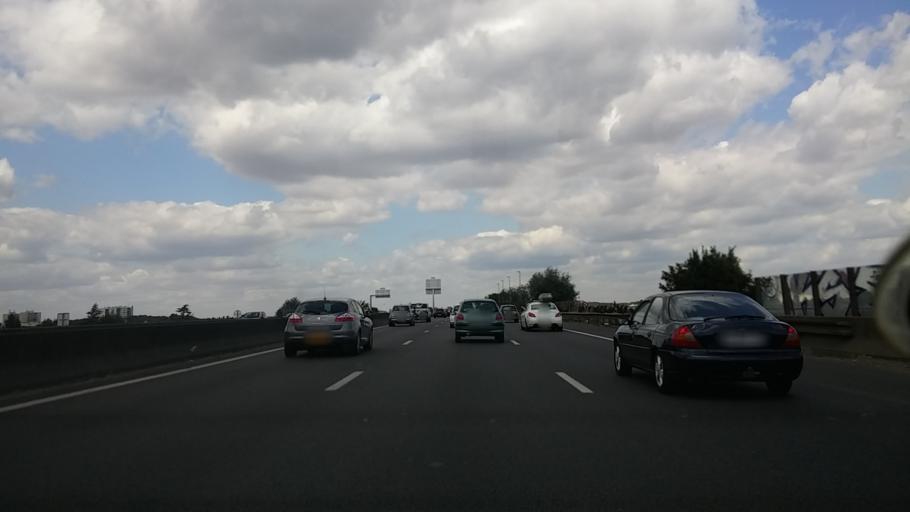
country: FR
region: Ile-de-France
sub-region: Departement de Seine-Saint-Denis
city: Aulnay-sous-Bois
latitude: 48.9308
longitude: 2.4813
